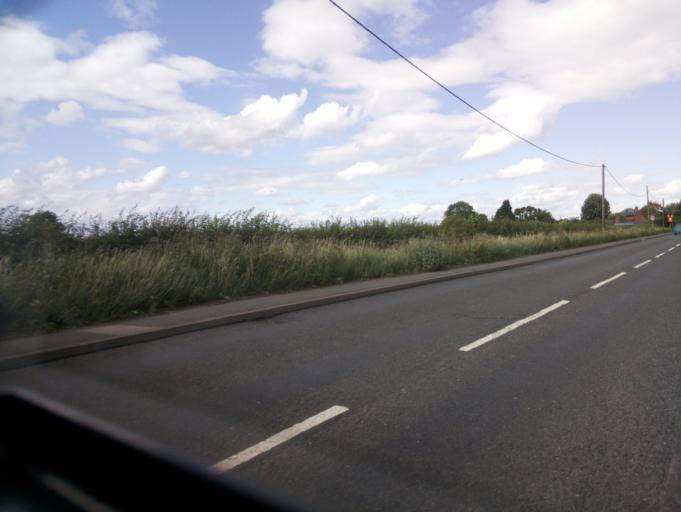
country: GB
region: England
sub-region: Leicestershire
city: Hathern
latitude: 52.8057
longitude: -1.2522
